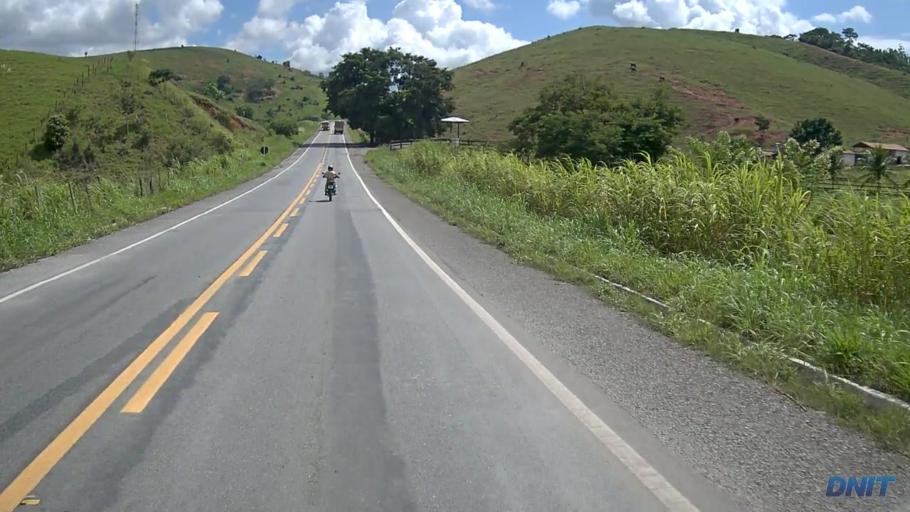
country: BR
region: Minas Gerais
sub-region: Governador Valadares
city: Governador Valadares
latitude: -19.0279
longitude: -42.1474
